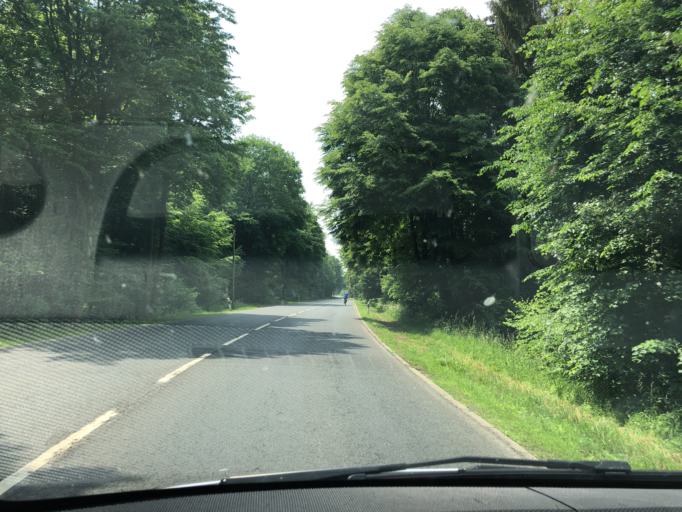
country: DE
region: Hesse
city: Stadtallendorf
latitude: 50.8325
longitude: 9.0528
